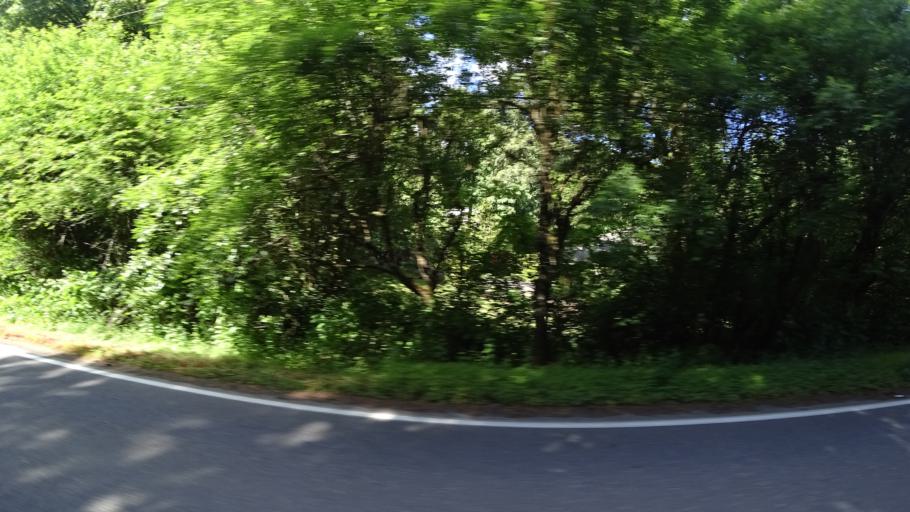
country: US
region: Oregon
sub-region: Washington County
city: Oak Hills
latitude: 45.5844
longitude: -122.8023
